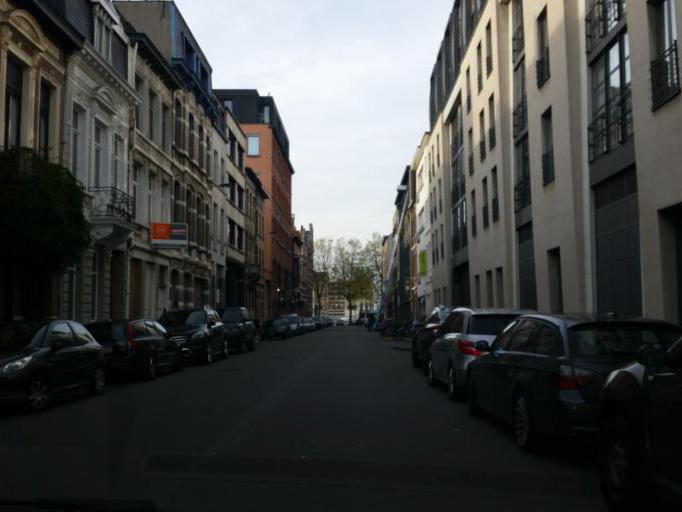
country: BE
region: Flanders
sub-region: Provincie Antwerpen
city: Antwerpen
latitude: 51.2089
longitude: 4.3924
